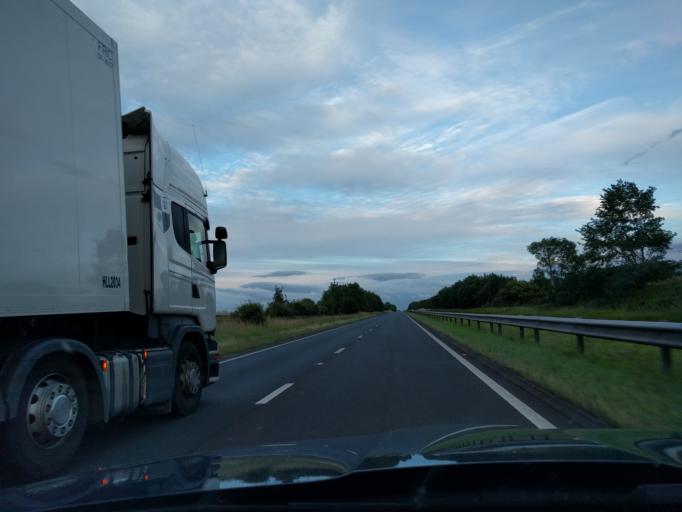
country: GB
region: England
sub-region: Northumberland
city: Morpeth
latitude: 55.1459
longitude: -1.6990
